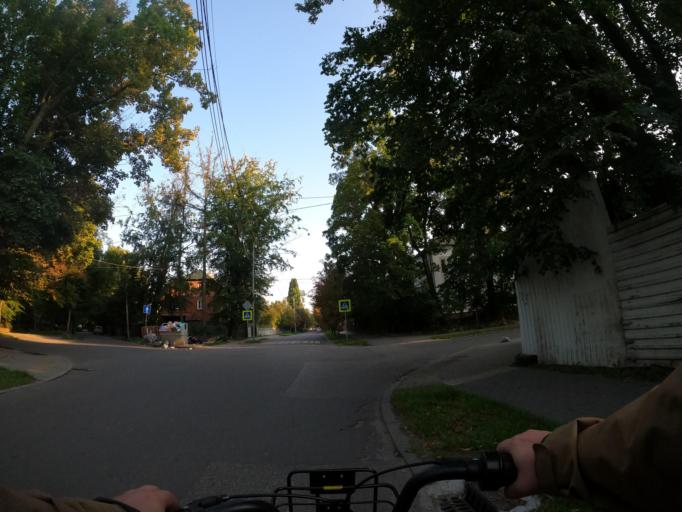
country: RU
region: Kaliningrad
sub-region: Gorod Kaliningrad
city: Kaliningrad
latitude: 54.7202
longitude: 20.4650
